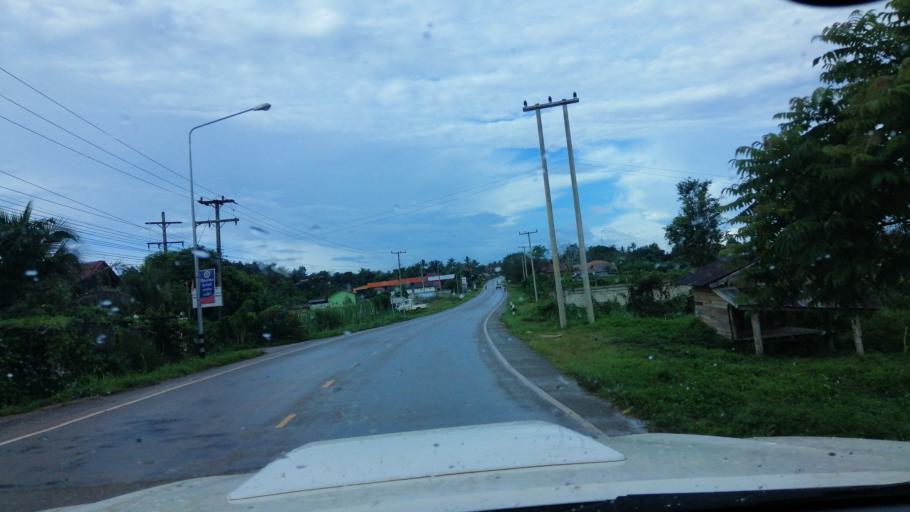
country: TH
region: Nan
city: Thung Chang
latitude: 19.6338
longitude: 100.8125
